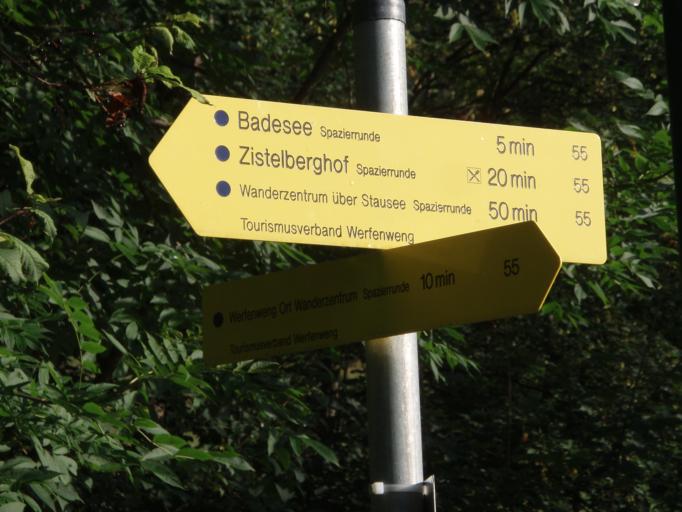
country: AT
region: Salzburg
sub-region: Politischer Bezirk Sankt Johann im Pongau
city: Werfenweng
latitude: 47.4641
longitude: 13.2567
